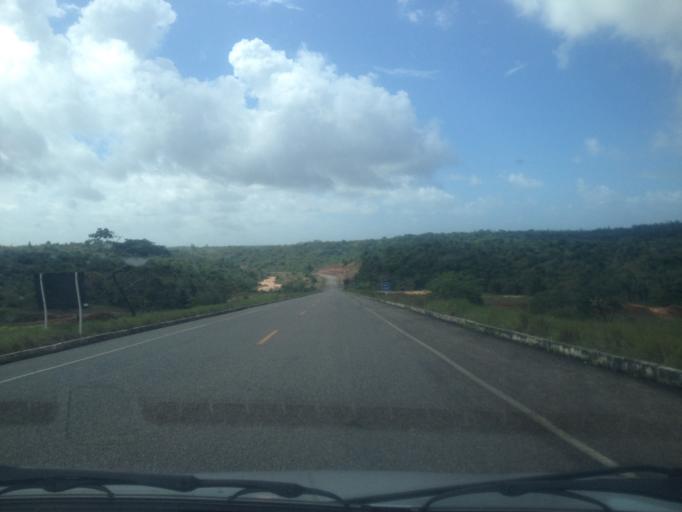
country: BR
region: Bahia
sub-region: Conde
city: Conde
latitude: -12.0778
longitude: -37.7573
